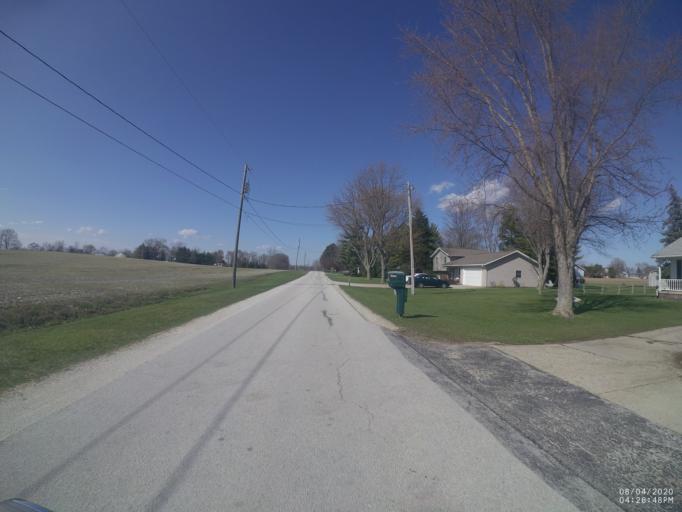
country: US
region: Ohio
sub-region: Sandusky County
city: Stony Prairie
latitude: 41.3244
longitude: -83.2058
